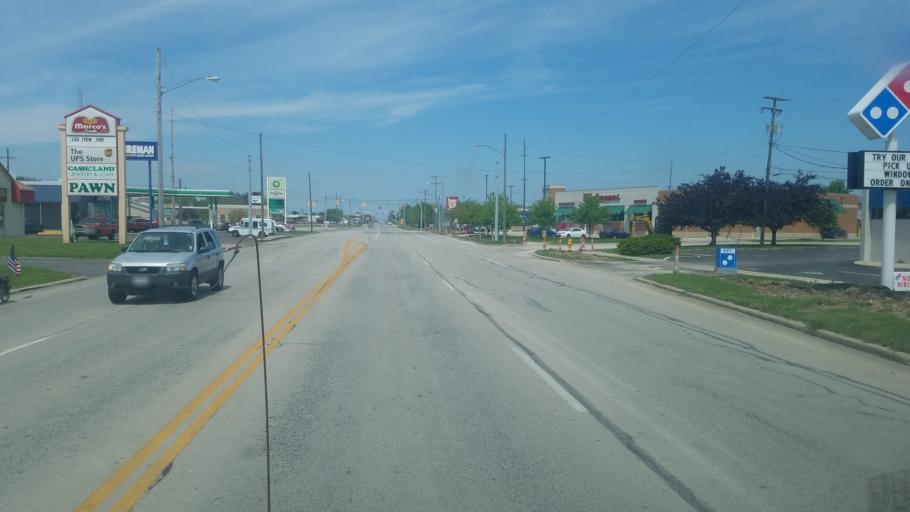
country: US
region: Ohio
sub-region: Sandusky County
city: Fremont
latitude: 41.3562
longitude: -83.1350
